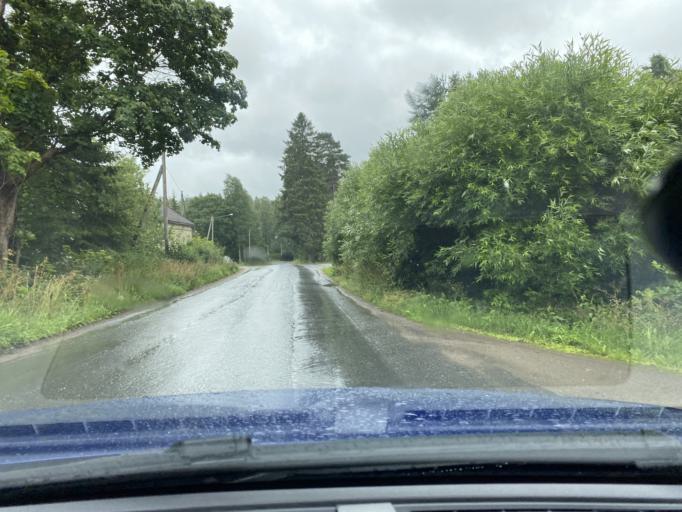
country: FI
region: Pirkanmaa
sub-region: Lounais-Pirkanmaa
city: Punkalaidun
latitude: 61.1476
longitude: 23.1931
